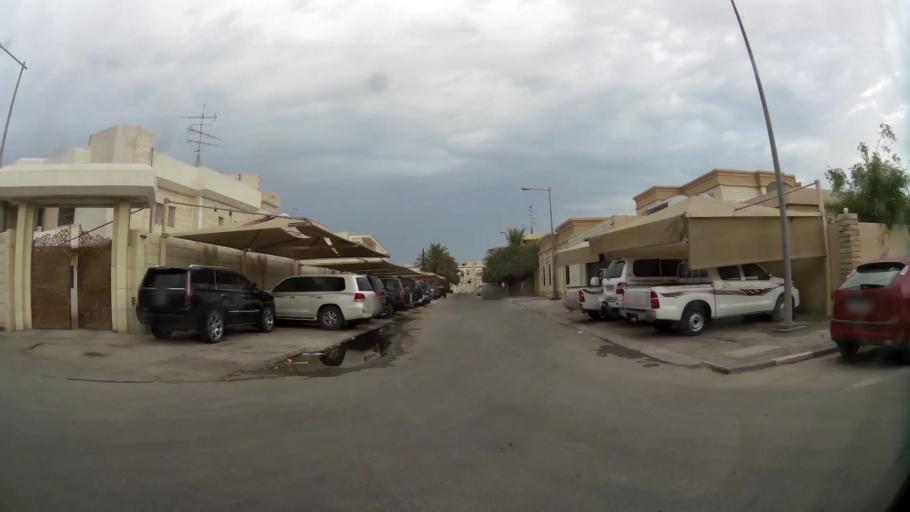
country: QA
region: Baladiyat ad Dawhah
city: Doha
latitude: 25.2693
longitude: 51.4983
